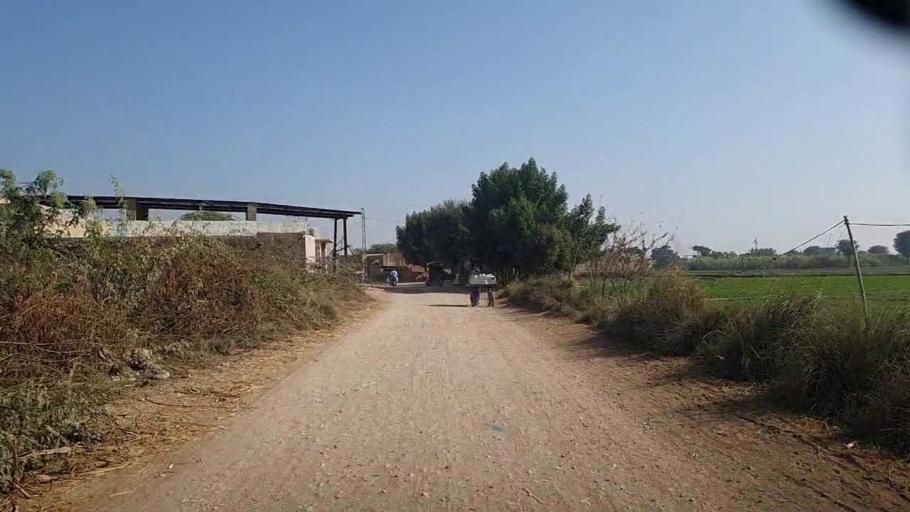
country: PK
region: Sindh
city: Darya Khan Marri
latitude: 26.6725
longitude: 68.3196
